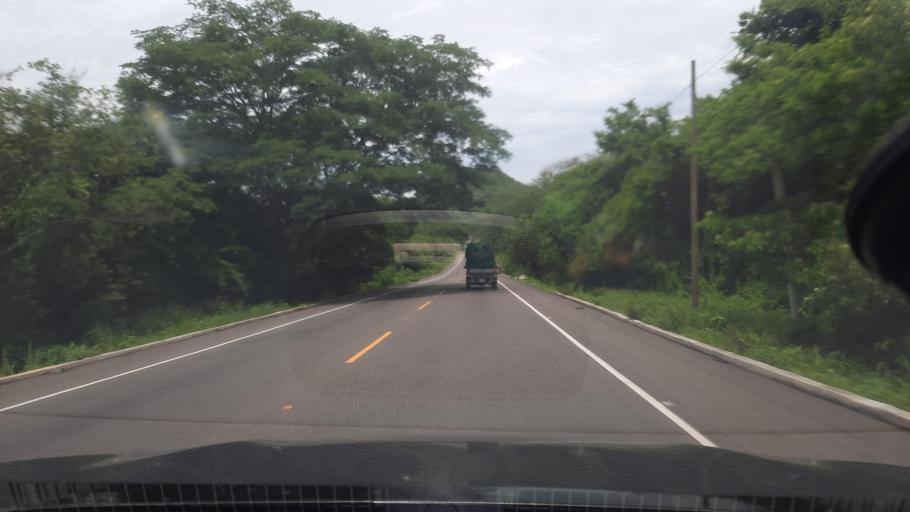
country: HN
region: Valle
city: Langue
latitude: 13.5750
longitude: -87.6762
